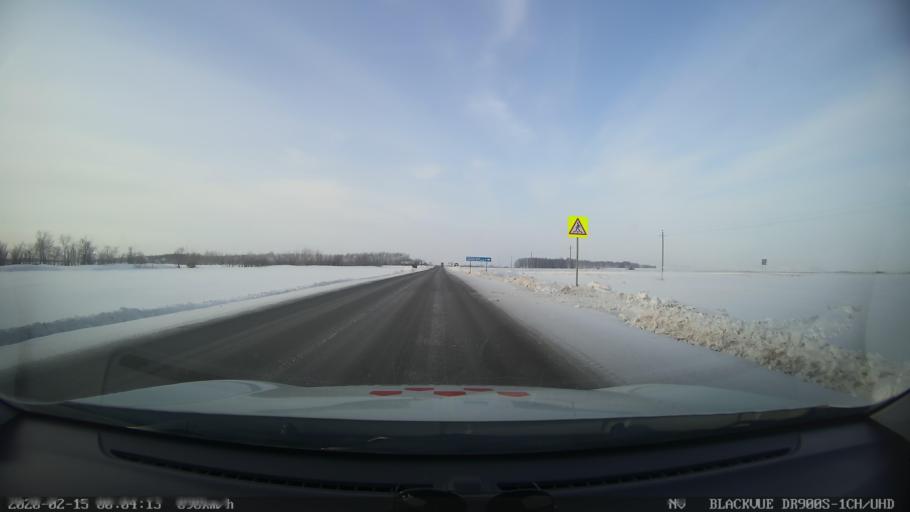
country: RU
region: Tatarstan
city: Kuybyshevskiy Zaton
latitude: 55.3801
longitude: 48.9867
